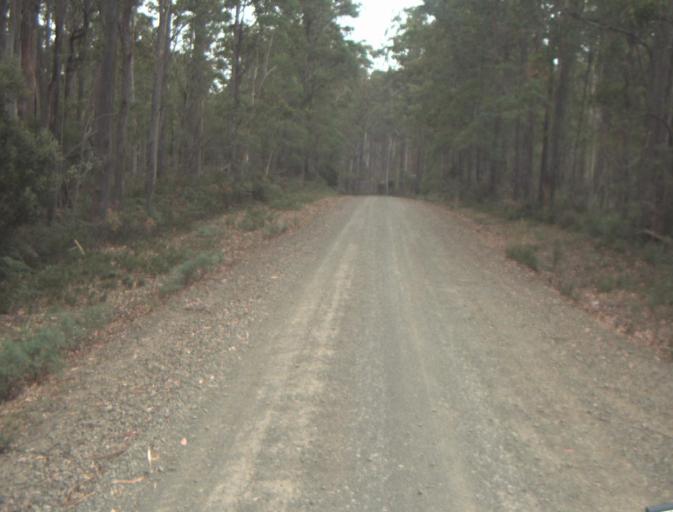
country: AU
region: Tasmania
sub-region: Dorset
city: Scottsdale
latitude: -41.4250
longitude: 147.5139
